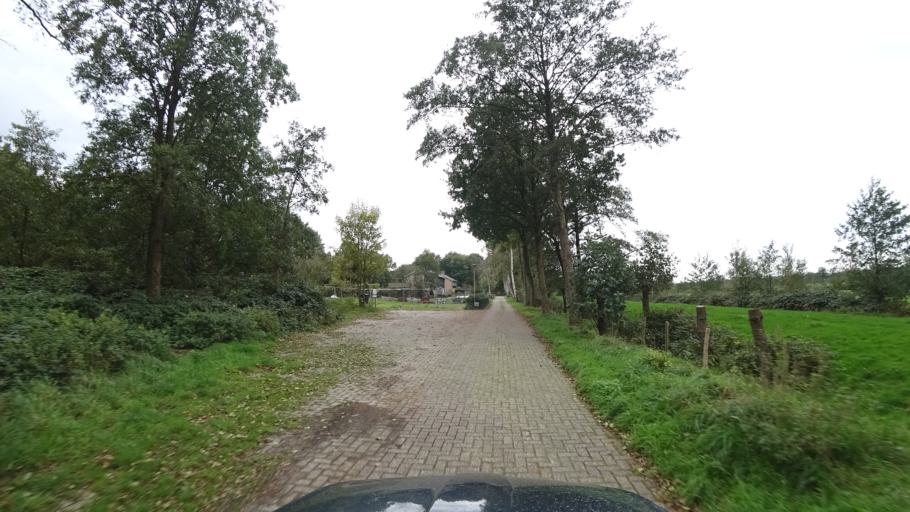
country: NL
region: Utrecht
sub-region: Gemeente De Bilt
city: De Bilt
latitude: 52.1539
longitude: 5.1895
